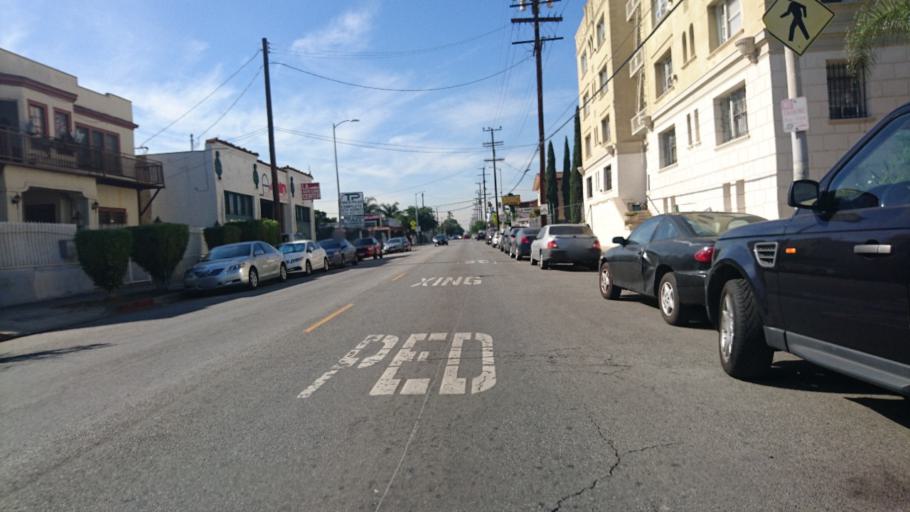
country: US
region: California
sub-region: Los Angeles County
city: Hollywood
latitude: 34.0952
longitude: -118.3016
